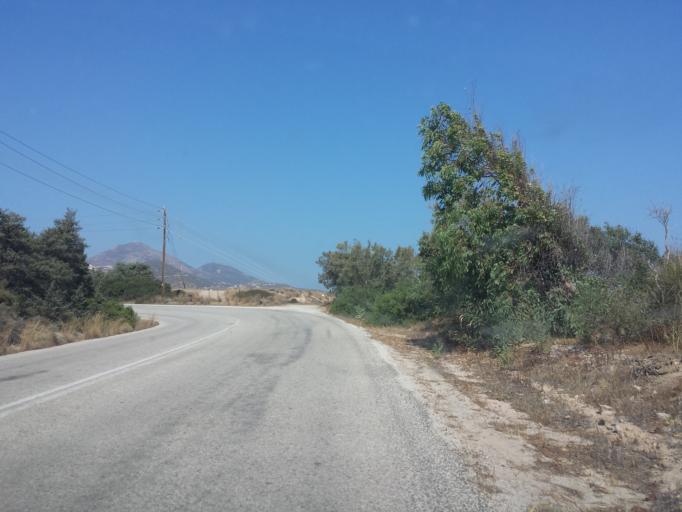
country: GR
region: South Aegean
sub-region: Nomos Kykladon
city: Adamas
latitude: 36.6891
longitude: 24.4515
